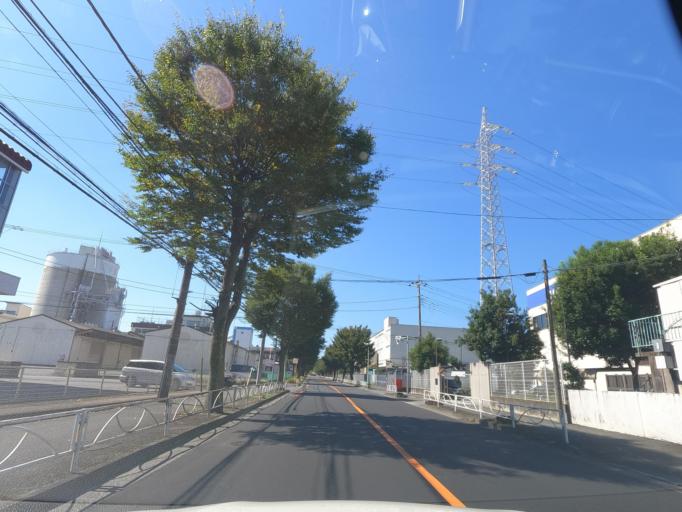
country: JP
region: Saitama
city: Sayama
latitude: 35.8801
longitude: 139.4378
